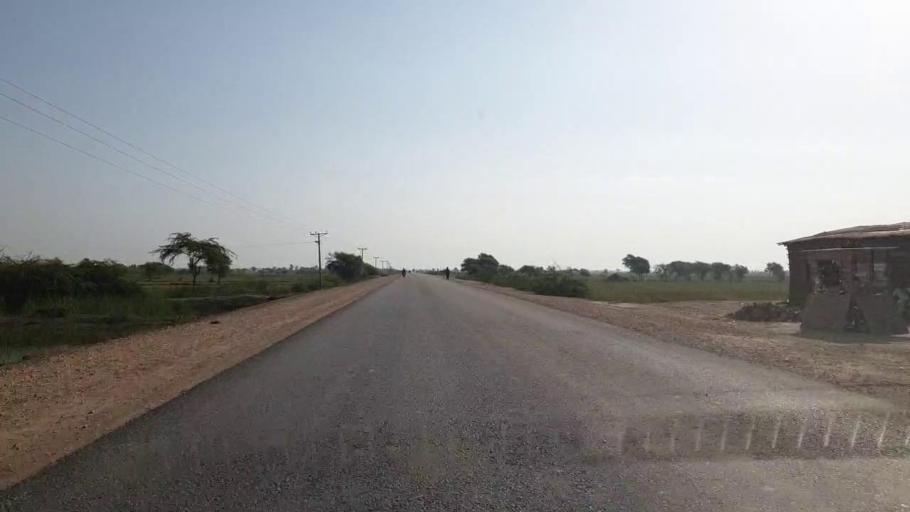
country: PK
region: Sindh
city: Tando Bago
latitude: 24.6577
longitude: 68.9836
